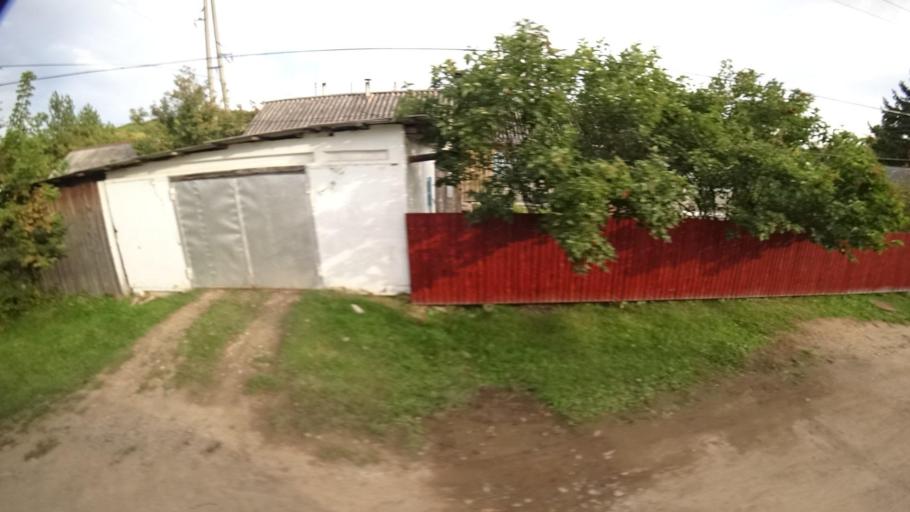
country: RU
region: Primorskiy
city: Yakovlevka
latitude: 44.4169
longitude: 133.4535
